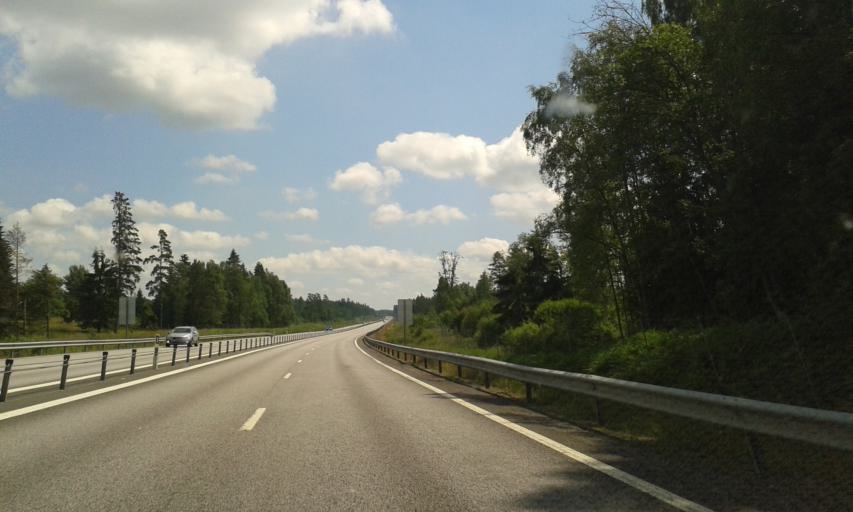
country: SE
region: Kronoberg
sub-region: Alvesta Kommun
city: Alvesta
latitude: 56.9196
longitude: 14.6095
